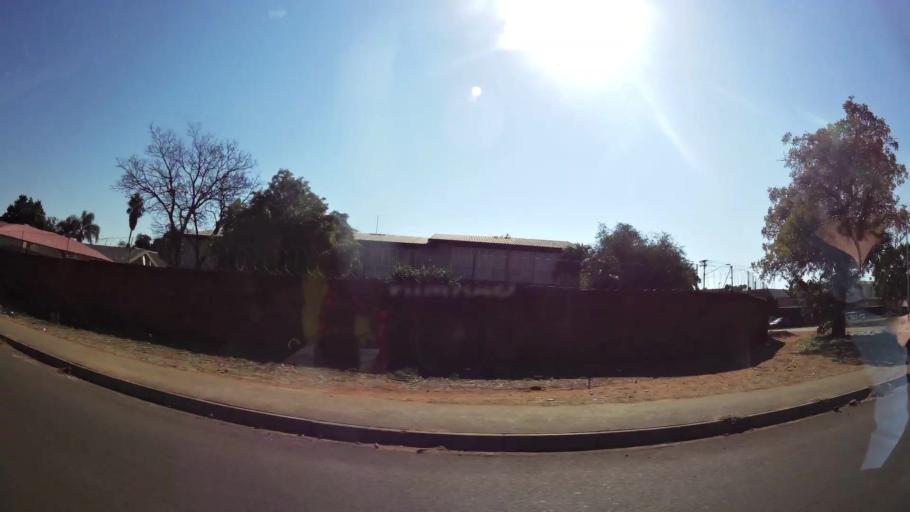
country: ZA
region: Gauteng
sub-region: City of Tshwane Metropolitan Municipality
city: Pretoria
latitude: -25.6834
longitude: 28.1966
